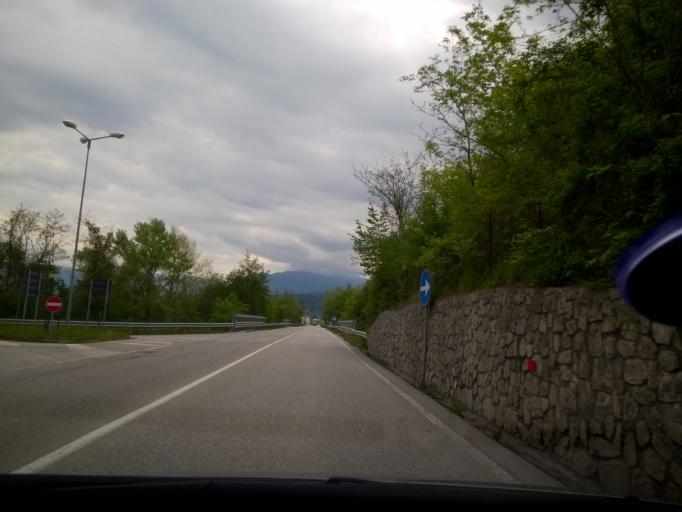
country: IT
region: Veneto
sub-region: Provincia di Belluno
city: Ponte nelle Alpi-Polpet
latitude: 46.1985
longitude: 12.2866
